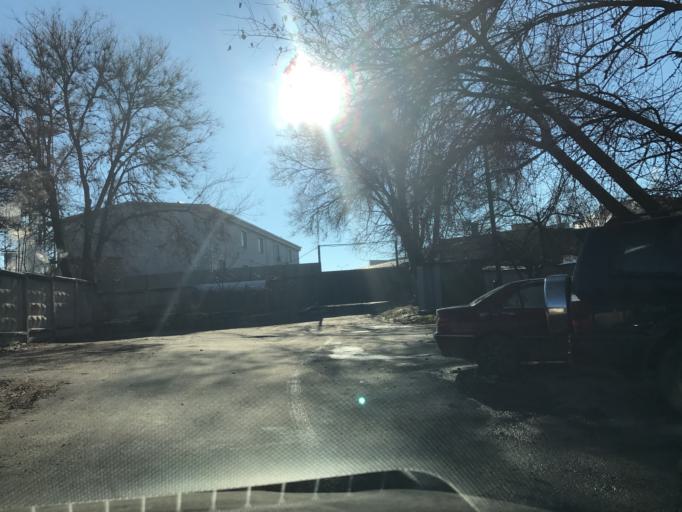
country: RU
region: Rostov
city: Rostov-na-Donu
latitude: 47.2427
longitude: 39.7387
